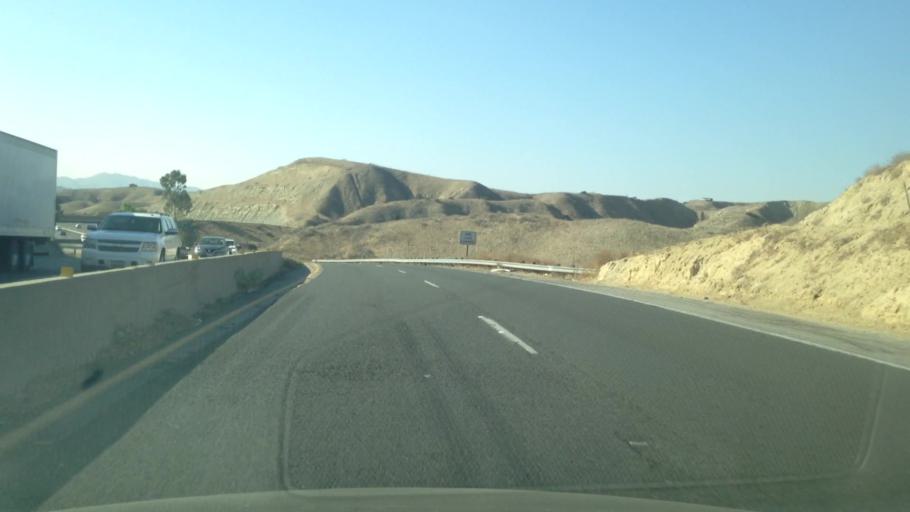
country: US
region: California
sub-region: Riverside County
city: Calimesa
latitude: 33.9376
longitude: -117.1232
